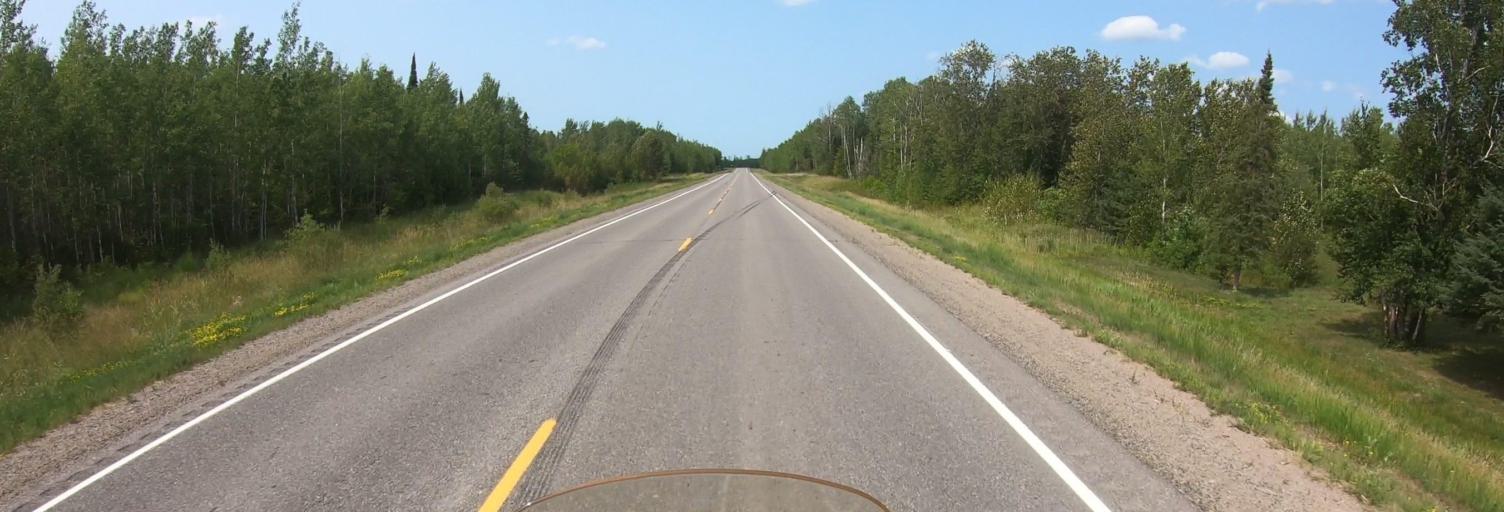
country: US
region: Minnesota
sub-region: Lake of the Woods County
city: Baudette
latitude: 48.6371
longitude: -94.1276
